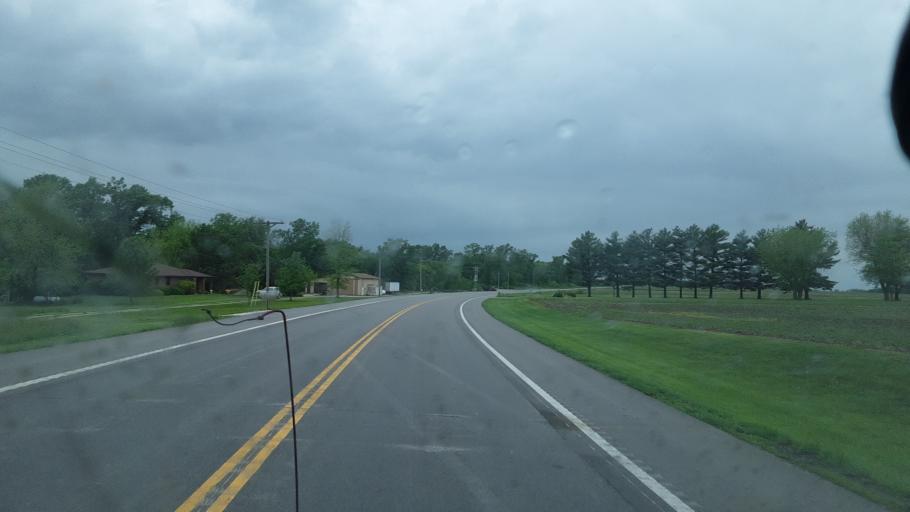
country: US
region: Missouri
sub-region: Marion County
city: Monroe City
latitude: 39.6010
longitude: -91.7448
